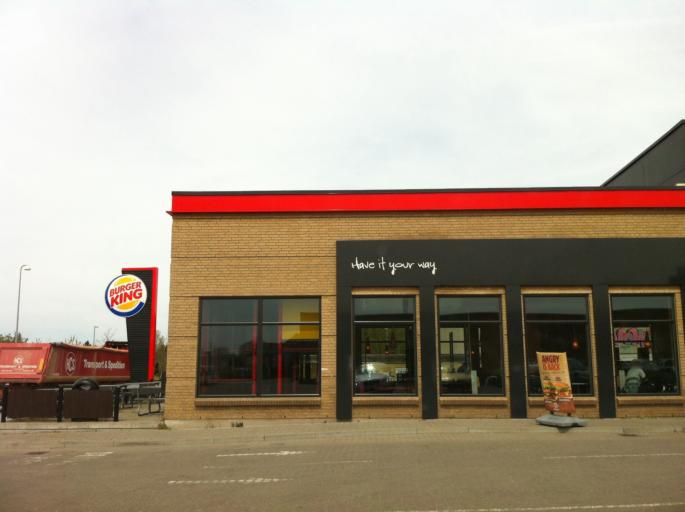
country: DK
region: Zealand
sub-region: Naestved Kommune
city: Naestved
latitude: 55.2386
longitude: 11.7779
